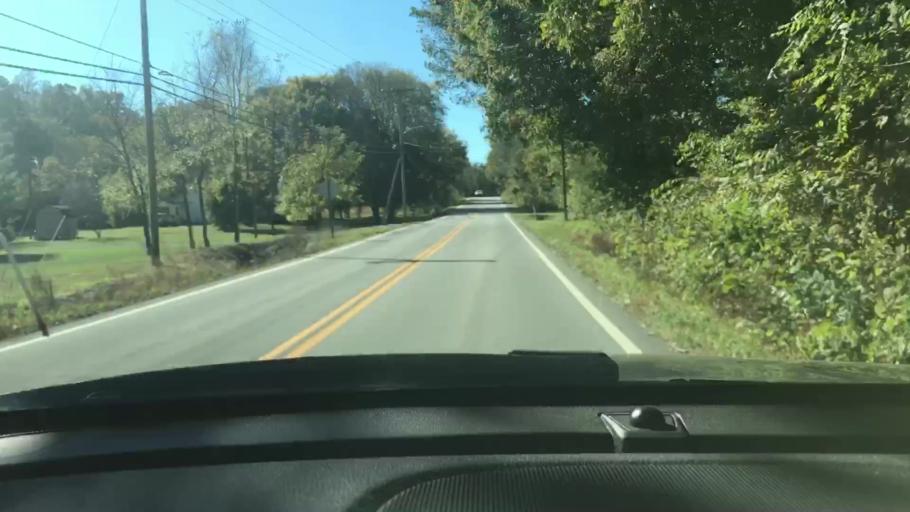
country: US
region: Tennessee
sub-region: Dickson County
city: Charlotte
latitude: 36.1812
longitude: -87.3218
